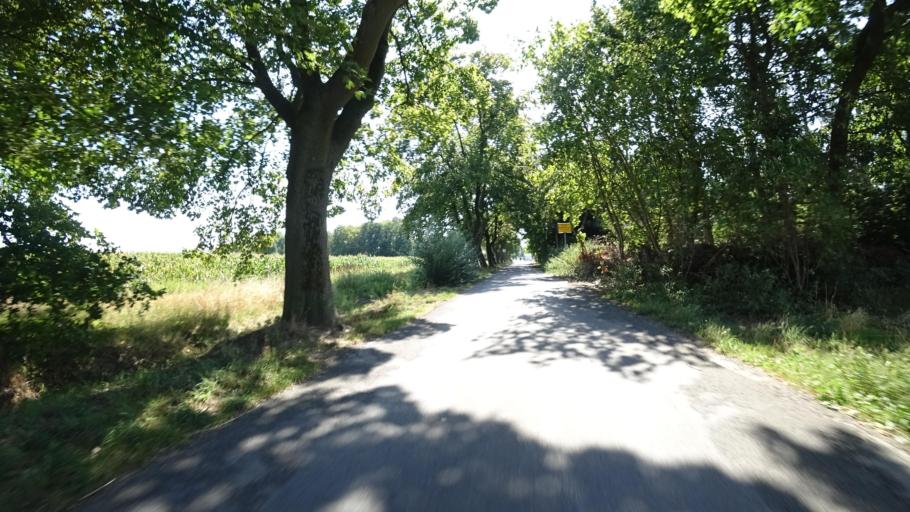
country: DE
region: North Rhine-Westphalia
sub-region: Regierungsbezirk Detmold
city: Rheda-Wiedenbruck
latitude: 51.8670
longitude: 8.2882
